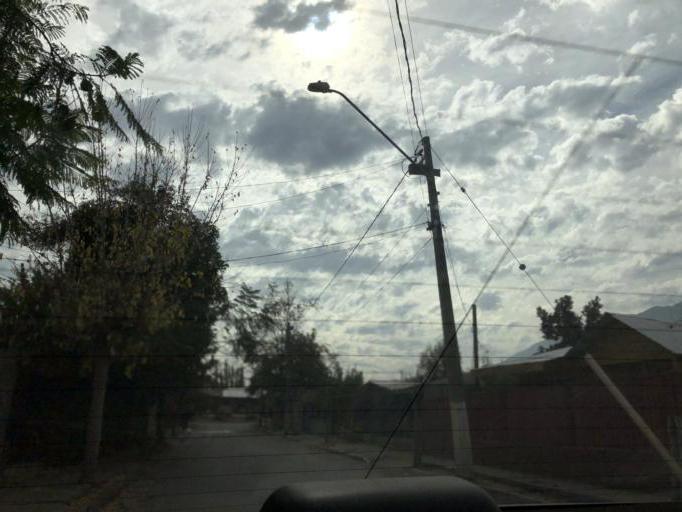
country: CL
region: Santiago Metropolitan
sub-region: Provincia de Cordillera
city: Puente Alto
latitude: -33.6126
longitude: -70.5192
